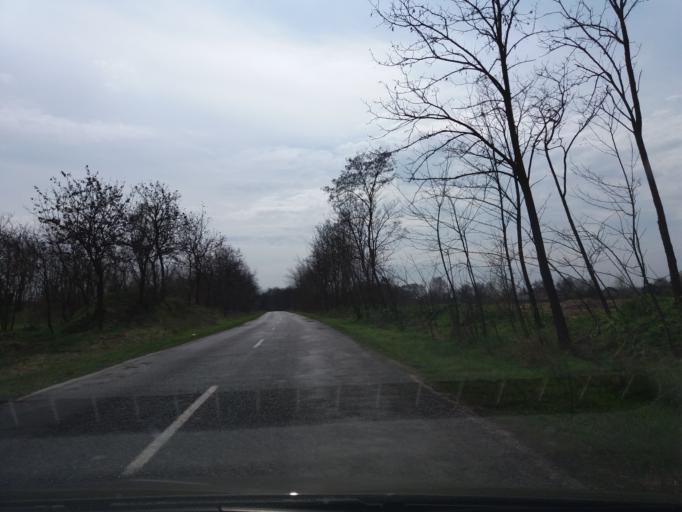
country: HU
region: Szabolcs-Szatmar-Bereg
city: Petnehaza
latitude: 48.0730
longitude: 22.0883
